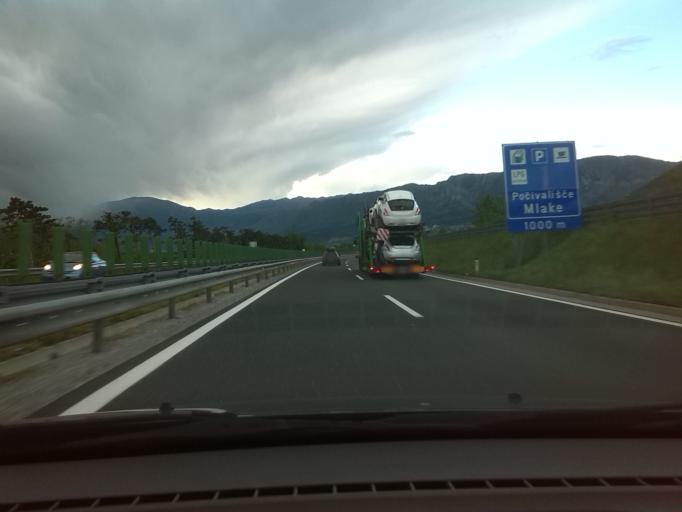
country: SI
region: Vipava
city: Vipava
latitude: 45.8182
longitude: 13.9624
